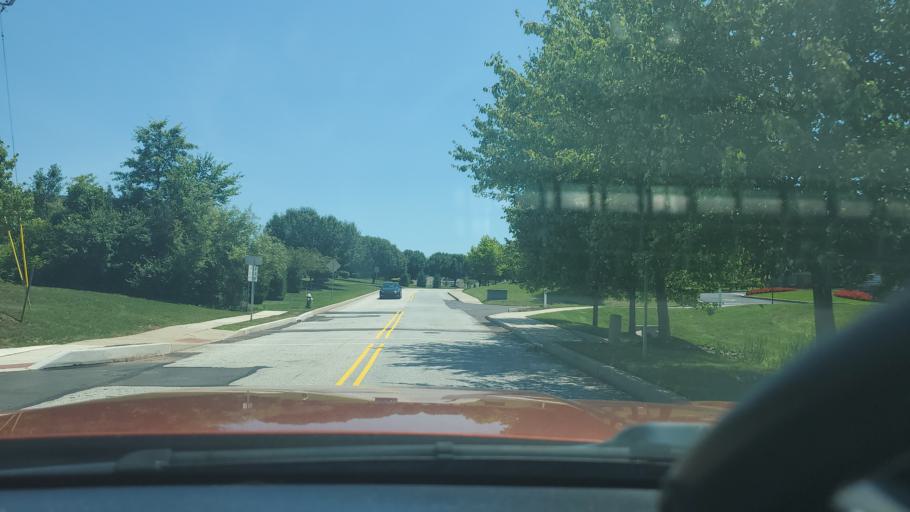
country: US
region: Pennsylvania
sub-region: Montgomery County
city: Limerick
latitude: 40.2168
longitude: -75.5533
